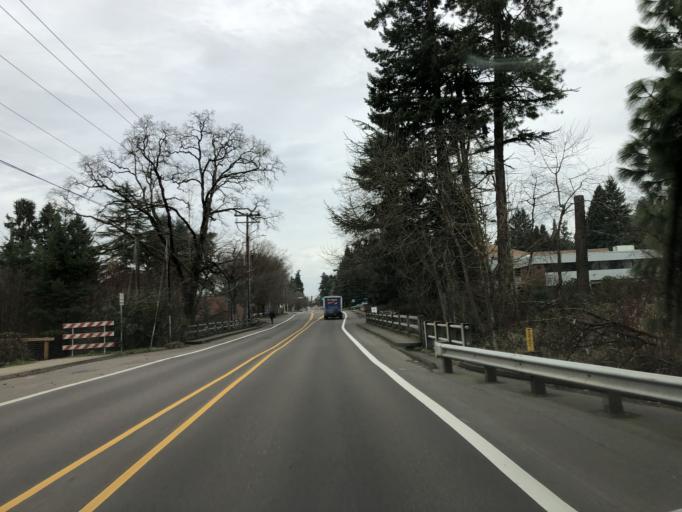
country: US
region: Oregon
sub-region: Washington County
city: Tigard
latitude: 45.4243
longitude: -122.7657
